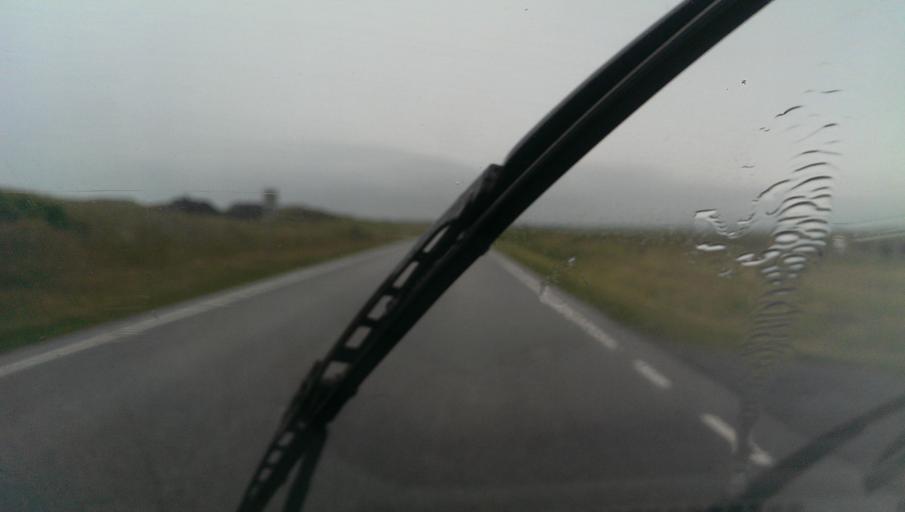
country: DK
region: Central Jutland
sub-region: Ringkobing-Skjern Kommune
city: Ringkobing
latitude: 56.2307
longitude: 8.1394
